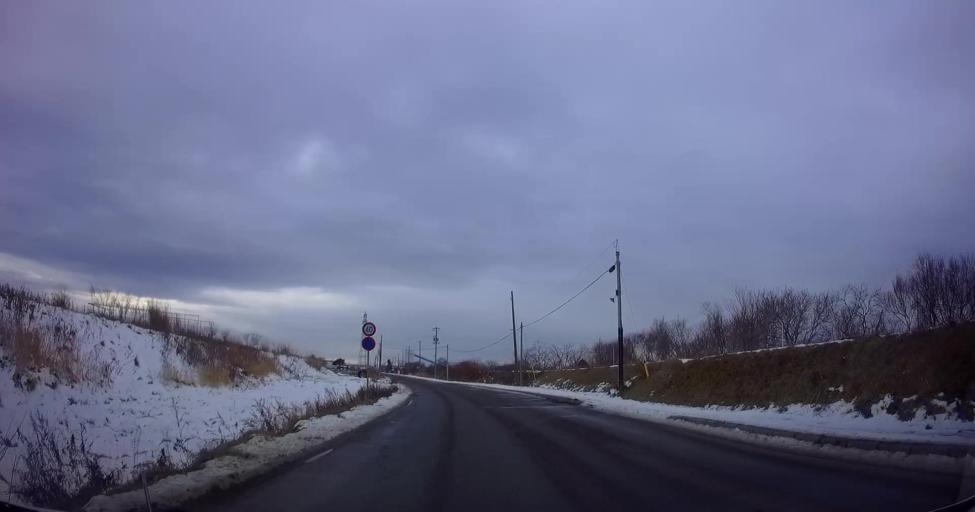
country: JP
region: Hokkaido
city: Kamiiso
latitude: 41.8337
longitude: 140.6896
